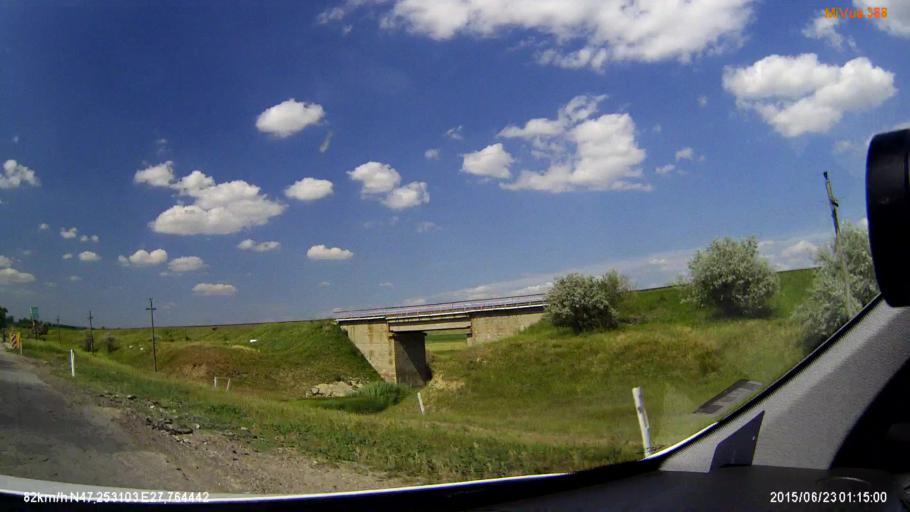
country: RO
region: Iasi
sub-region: Comuna Ungheni
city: Bosia
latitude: 47.2529
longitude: 27.7646
